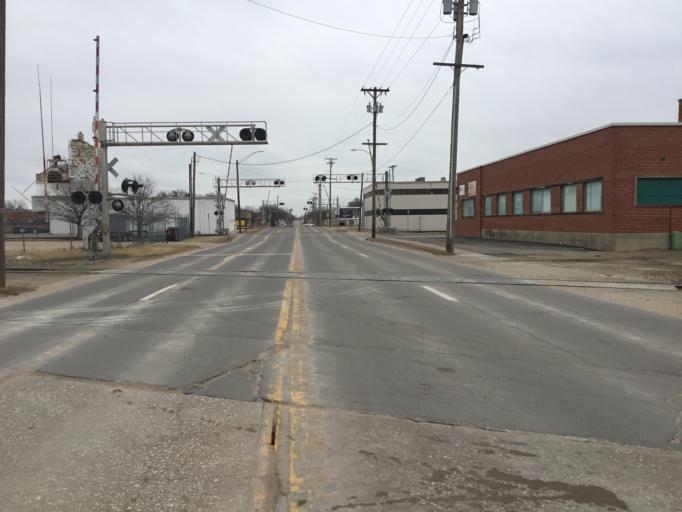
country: US
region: Kansas
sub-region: Sedgwick County
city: Wichita
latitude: 37.6716
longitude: -97.3299
